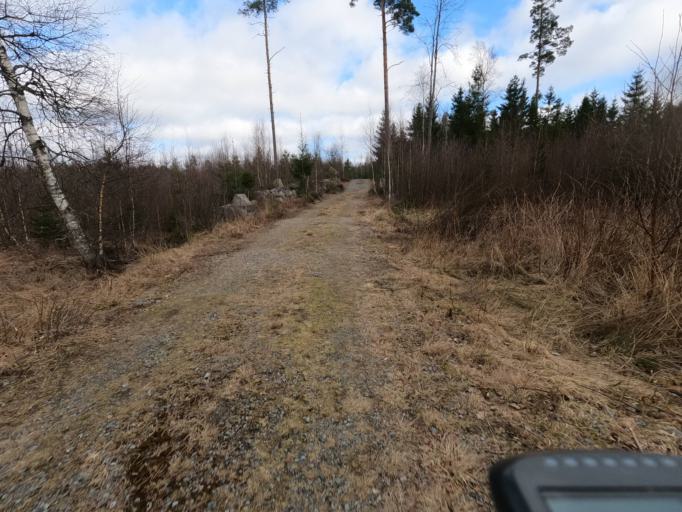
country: SE
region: Kronoberg
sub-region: Alvesta Kommun
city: Vislanda
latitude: 56.8111
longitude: 14.3944
